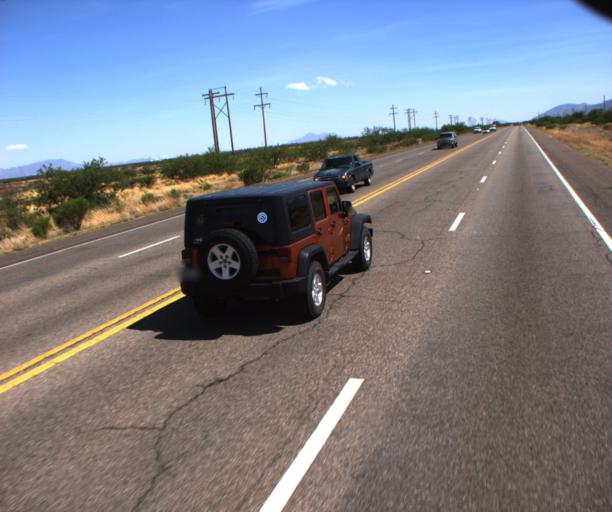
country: US
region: Arizona
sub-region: Cochise County
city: Huachuca City
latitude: 31.6007
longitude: -110.3276
